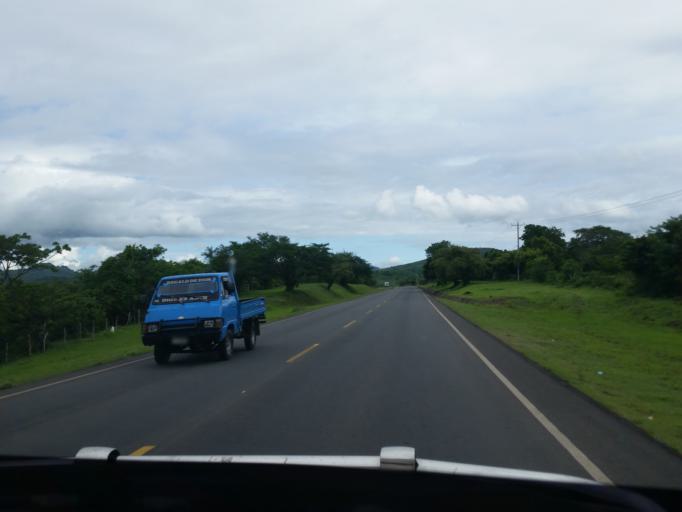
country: NI
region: Managua
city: Tipitapa
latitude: 12.4101
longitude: -86.0422
